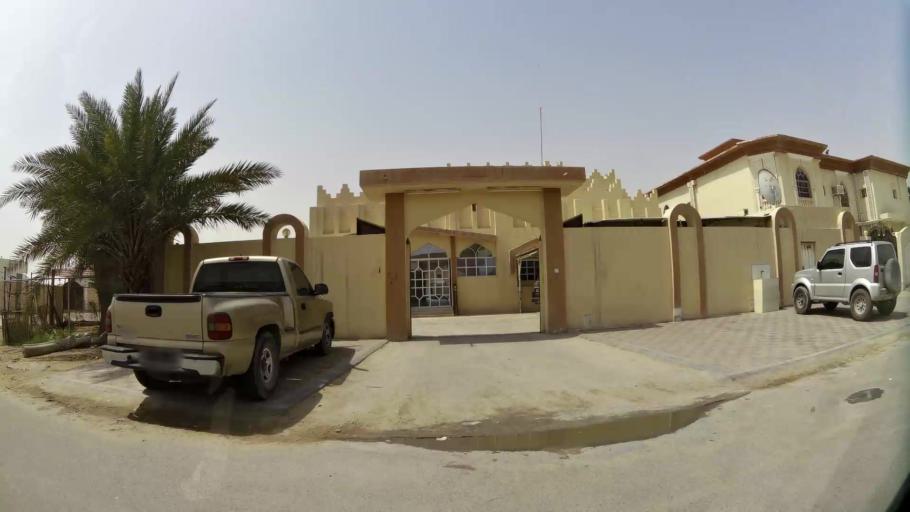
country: QA
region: Baladiyat ar Rayyan
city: Ar Rayyan
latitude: 25.2360
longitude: 51.4197
